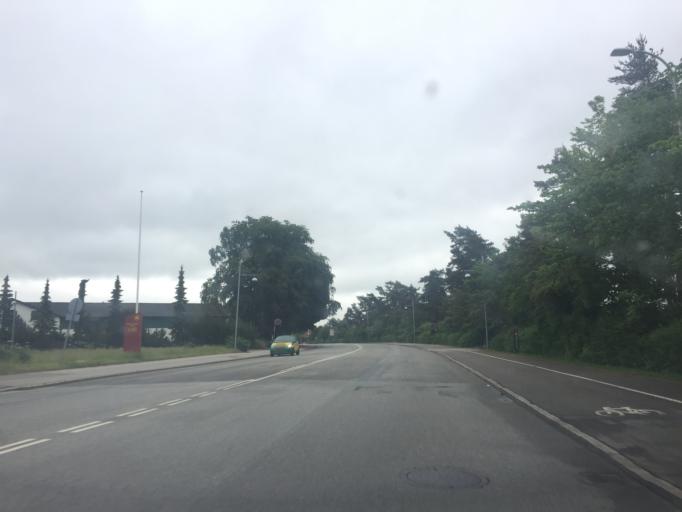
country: DK
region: Capital Region
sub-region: Glostrup Kommune
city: Glostrup
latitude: 55.6756
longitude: 12.3908
